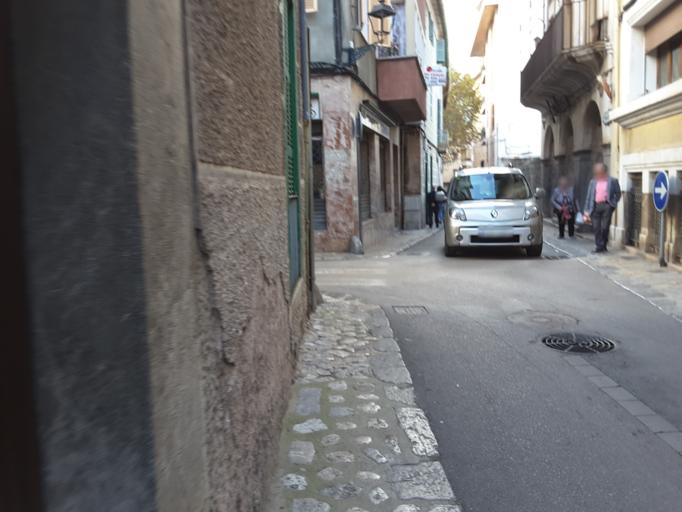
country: ES
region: Balearic Islands
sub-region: Illes Balears
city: Soller
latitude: 39.7658
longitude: 2.7166
